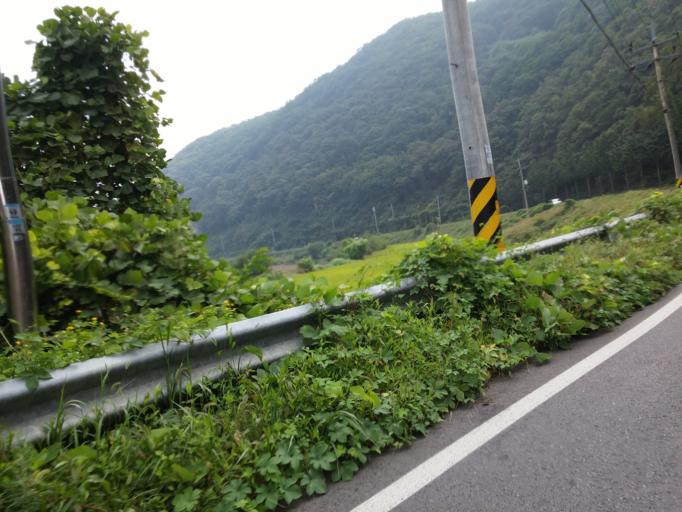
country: KR
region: Chungcheongbuk-do
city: Yong-dong
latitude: 36.3991
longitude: 127.8030
